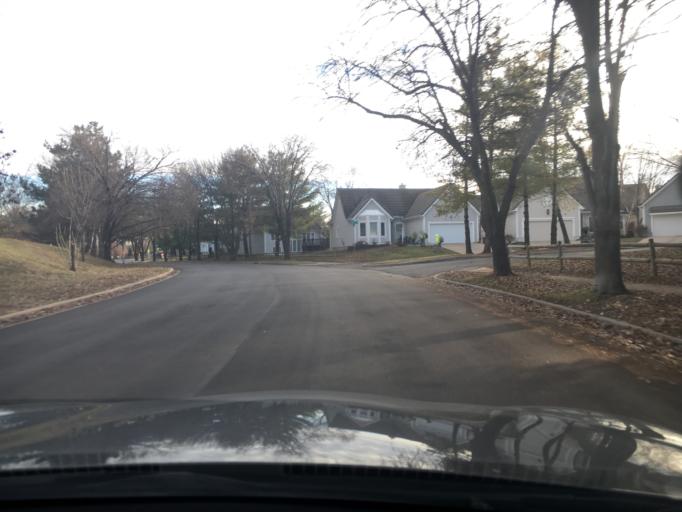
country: US
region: Kansas
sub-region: Johnson County
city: Leawood
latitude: 38.9075
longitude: -94.6106
